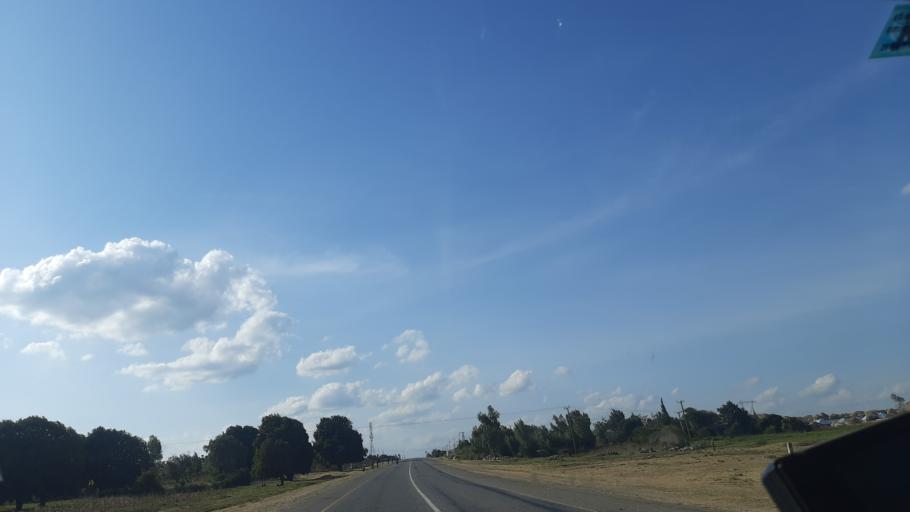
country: TZ
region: Singida
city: Puma
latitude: -5.0108
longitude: 34.7575
